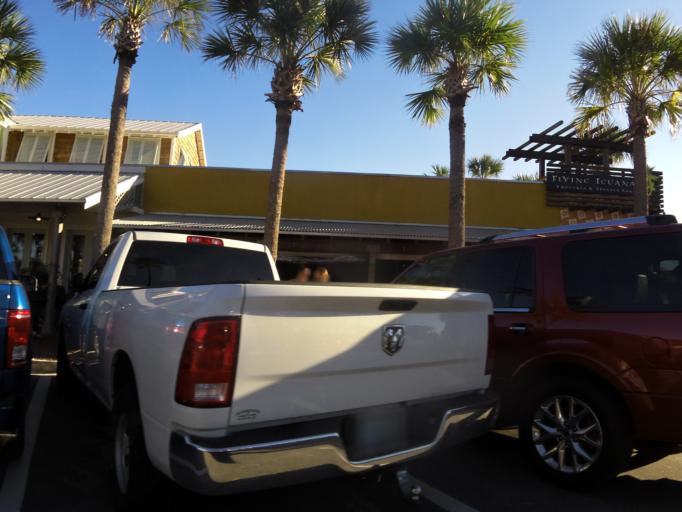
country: US
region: Florida
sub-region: Duval County
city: Atlantic Beach
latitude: 30.3246
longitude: -81.3965
